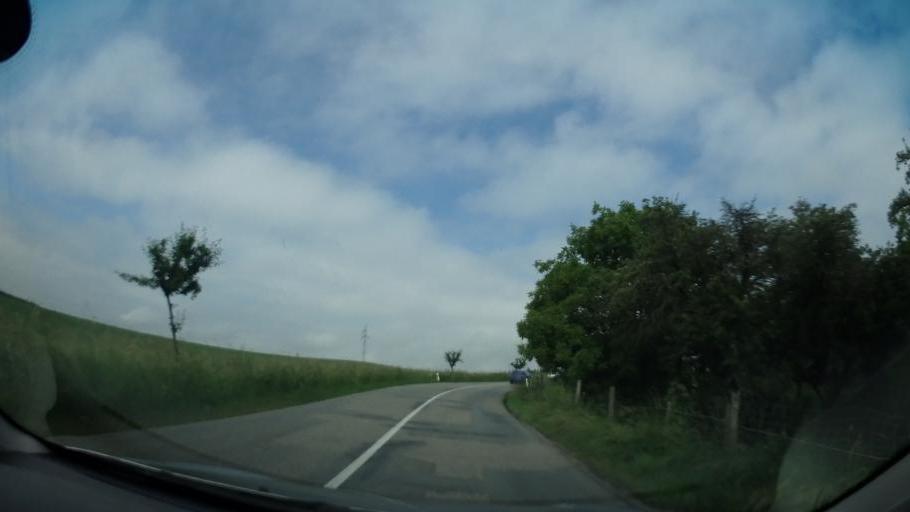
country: CZ
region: South Moravian
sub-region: Okres Brno-Venkov
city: Dolni Loucky
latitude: 49.3792
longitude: 16.3474
